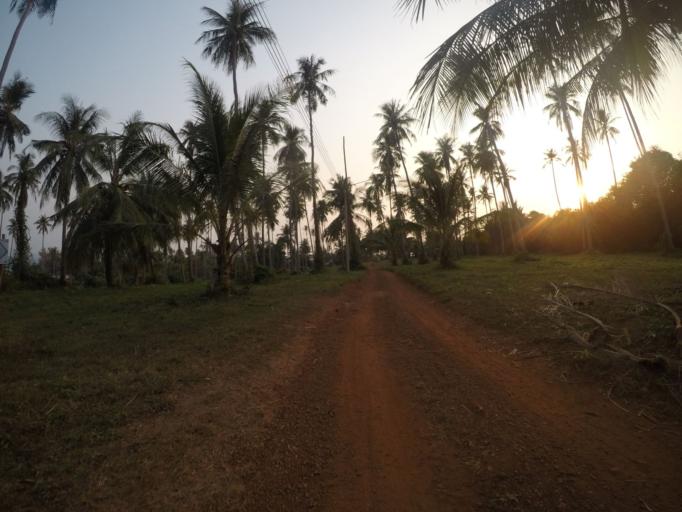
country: TH
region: Trat
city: Ko Kut
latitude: 11.7946
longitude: 102.4876
